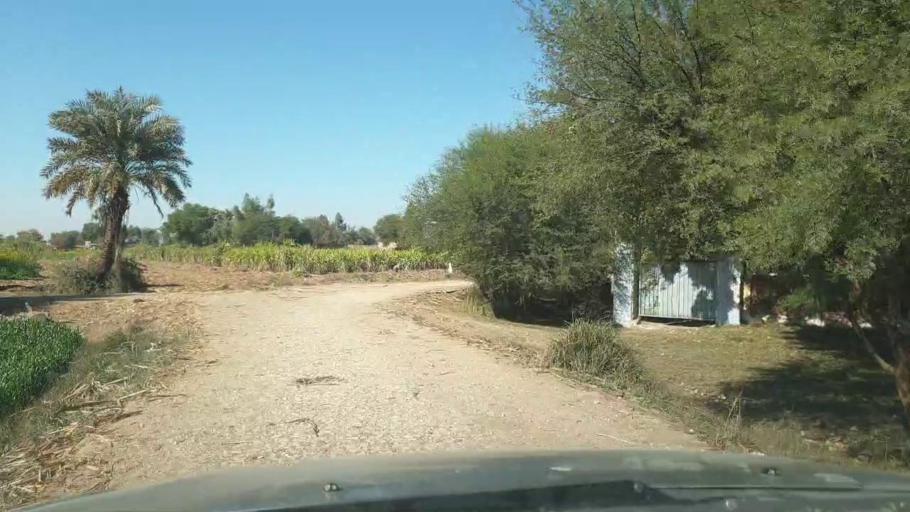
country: PK
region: Sindh
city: Ghotki
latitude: 28.0549
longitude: 69.2452
